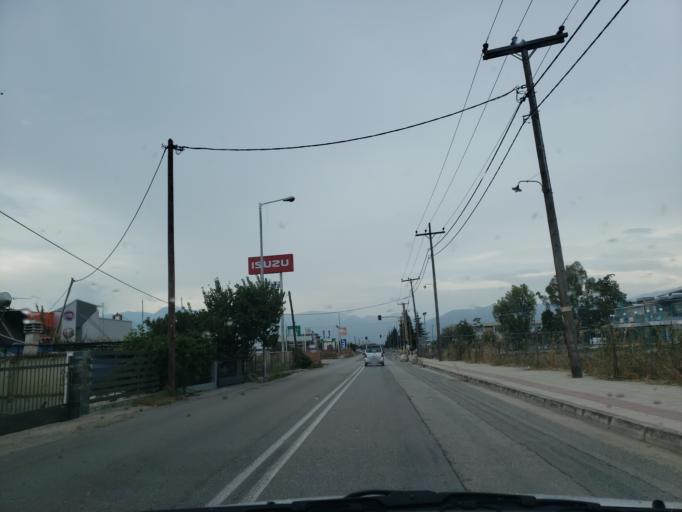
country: GR
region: Central Greece
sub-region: Nomos Fthiotidos
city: Lamia
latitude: 38.8770
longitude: 22.4392
